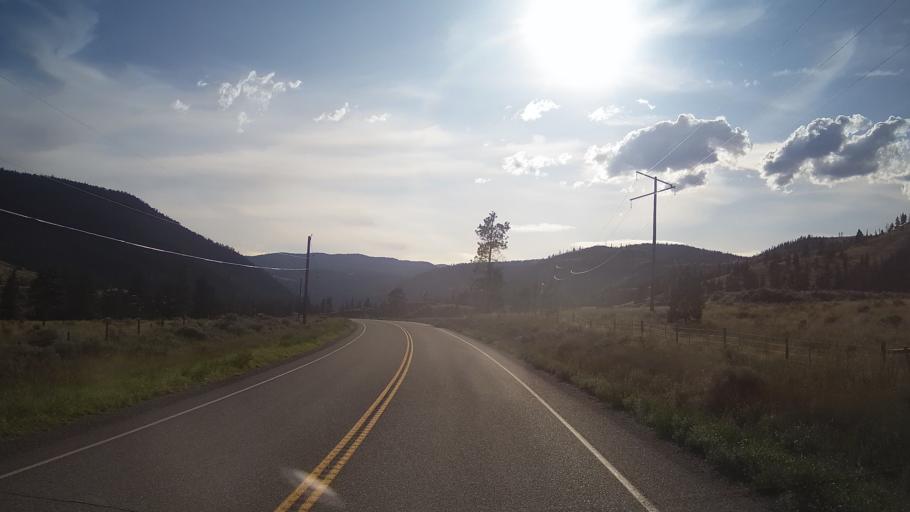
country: CA
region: British Columbia
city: Cache Creek
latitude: 50.8872
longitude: -121.4641
